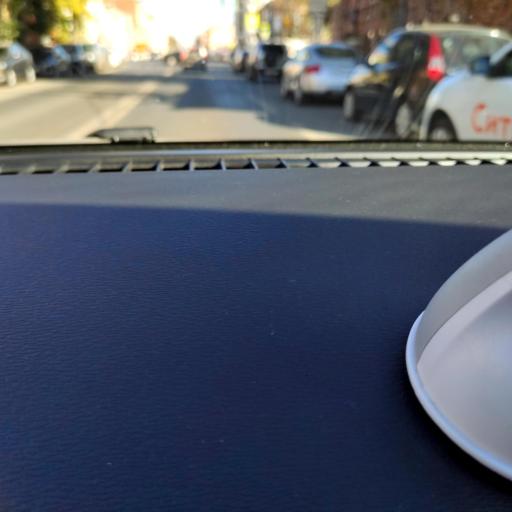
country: RU
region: Samara
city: Samara
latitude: 53.1826
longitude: 50.0959
